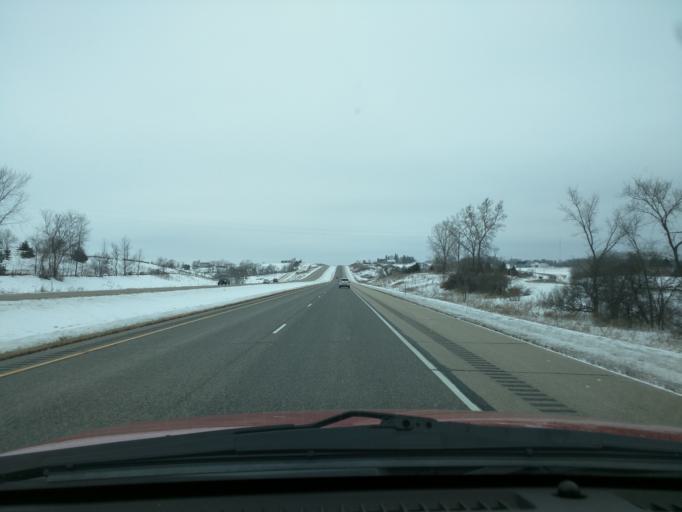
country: US
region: Minnesota
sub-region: Winona County
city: Winona
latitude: 43.9444
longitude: -91.6381
